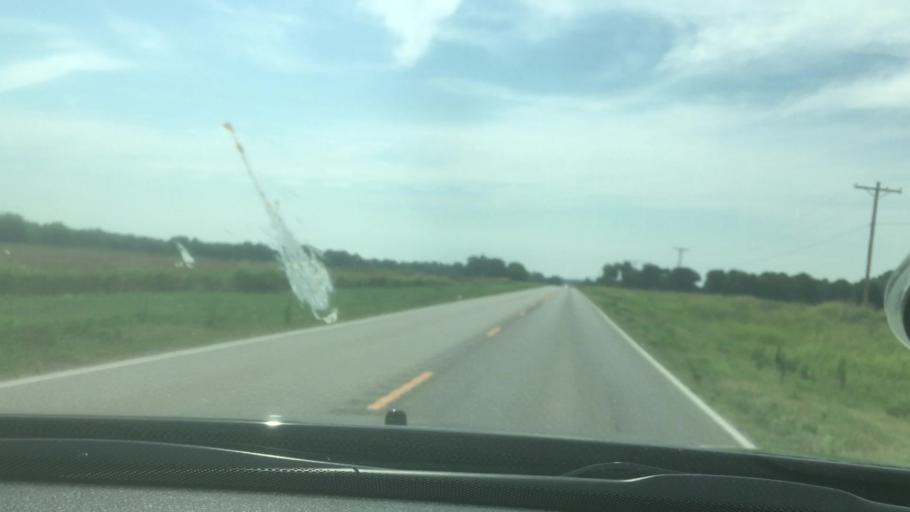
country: US
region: Oklahoma
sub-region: Garvin County
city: Maysville
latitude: 34.7931
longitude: -97.3502
